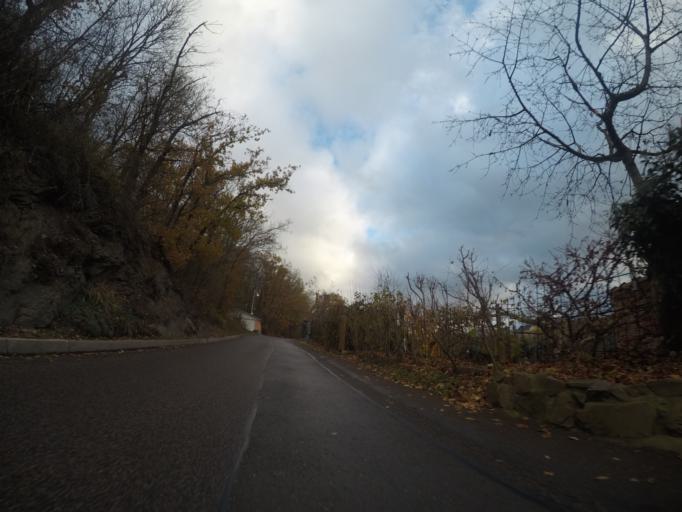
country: DE
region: Thuringia
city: Vollmershain
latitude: 50.8540
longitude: 12.2883
